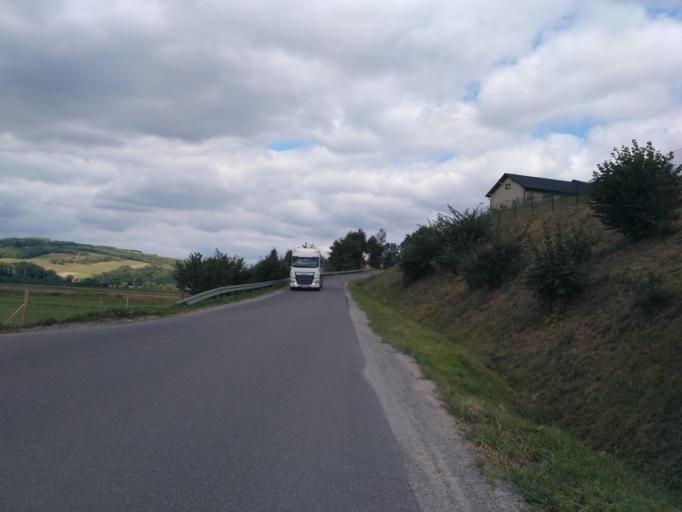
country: PL
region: Subcarpathian Voivodeship
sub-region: Powiat brzozowski
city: Nozdrzec
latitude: 49.7715
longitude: 22.2233
